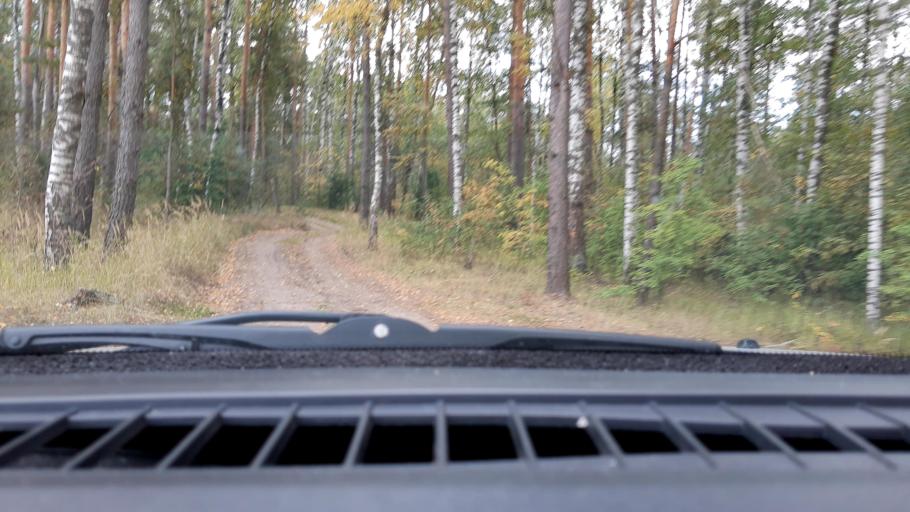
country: RU
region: Nizjnij Novgorod
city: Gorbatovka
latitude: 56.3129
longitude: 43.7192
